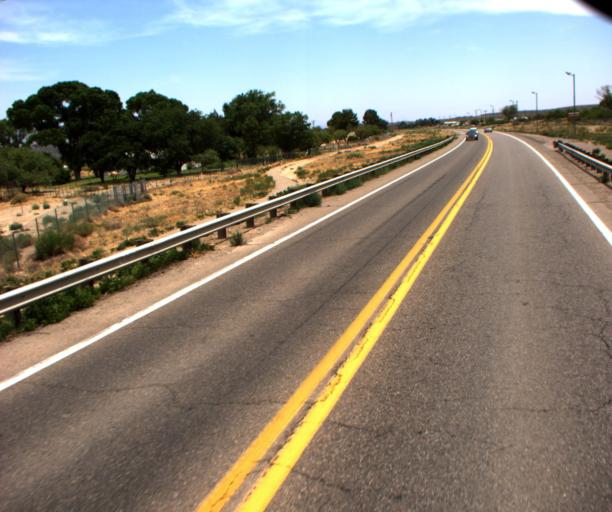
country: US
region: Arizona
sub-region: Graham County
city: Bylas
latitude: 33.1175
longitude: -110.1078
